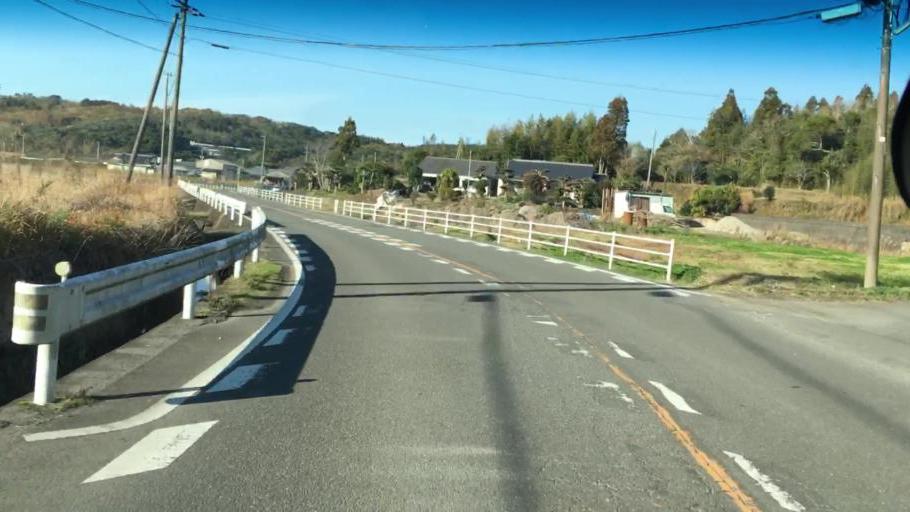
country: JP
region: Kagoshima
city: Satsumasendai
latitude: 31.8277
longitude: 130.2470
